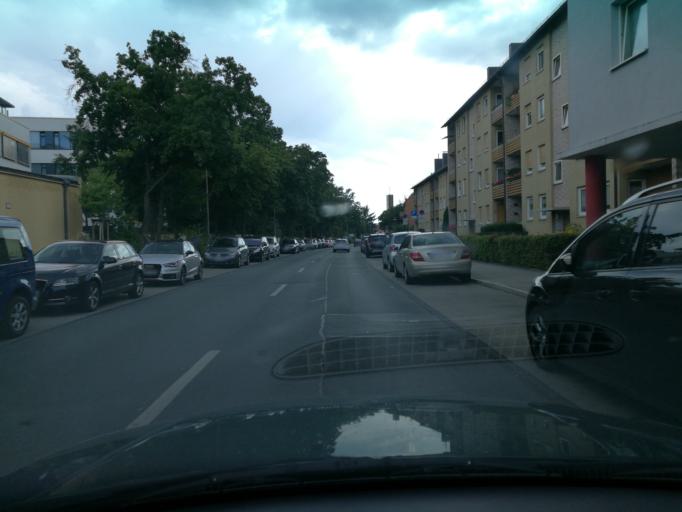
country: DE
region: Bavaria
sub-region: Regierungsbezirk Mittelfranken
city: Furth
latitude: 49.4858
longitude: 10.9730
